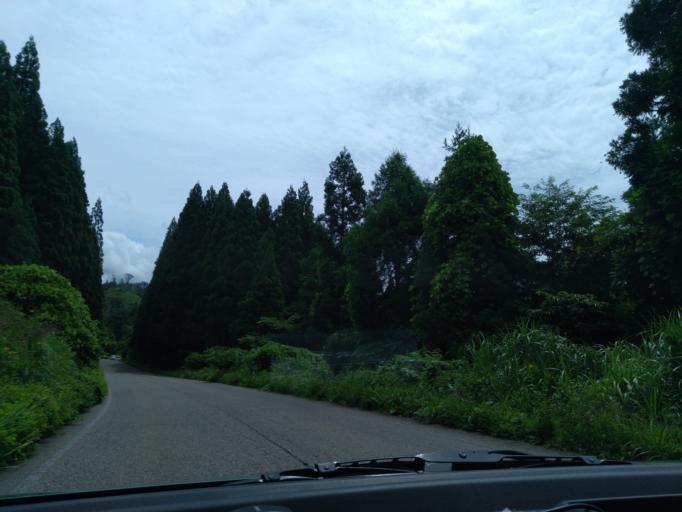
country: JP
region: Akita
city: Kakunodatemachi
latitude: 39.5711
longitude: 140.6340
